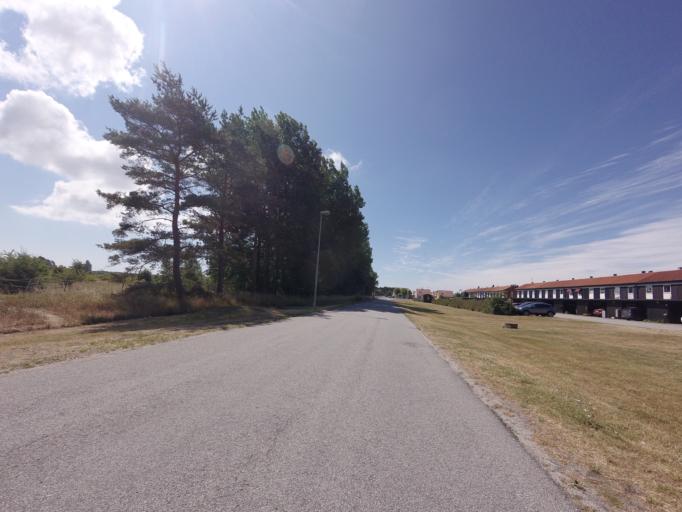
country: SE
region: Skane
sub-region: Vellinge Kommun
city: Skanor med Falsterbo
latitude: 55.4177
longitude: 12.8627
